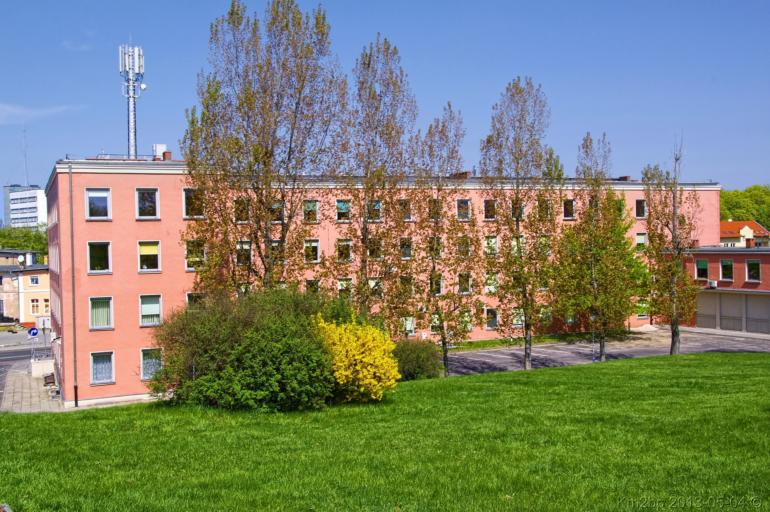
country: PL
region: Lubusz
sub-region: Zielona Gora
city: Zielona Gora
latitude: 51.9387
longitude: 15.5121
